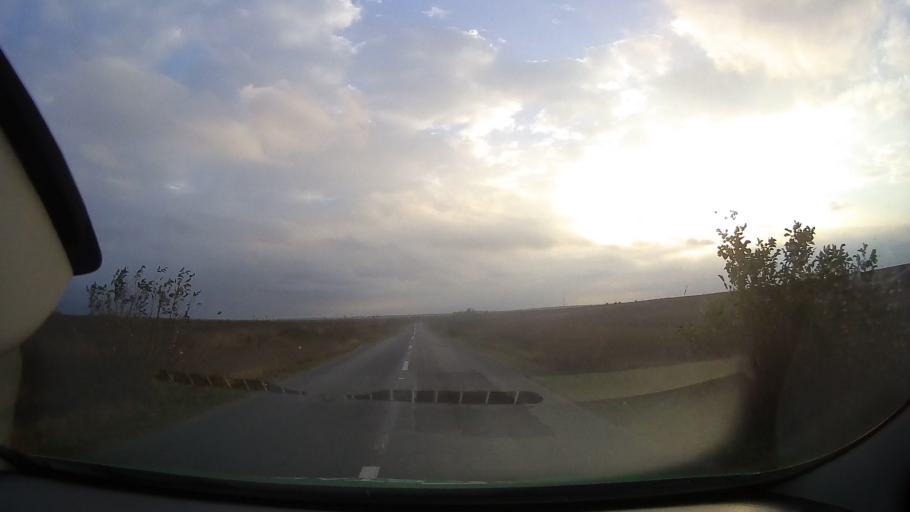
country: RO
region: Constanta
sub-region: Comuna Adamclisi
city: Adamclisi
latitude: 44.0212
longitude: 27.9069
